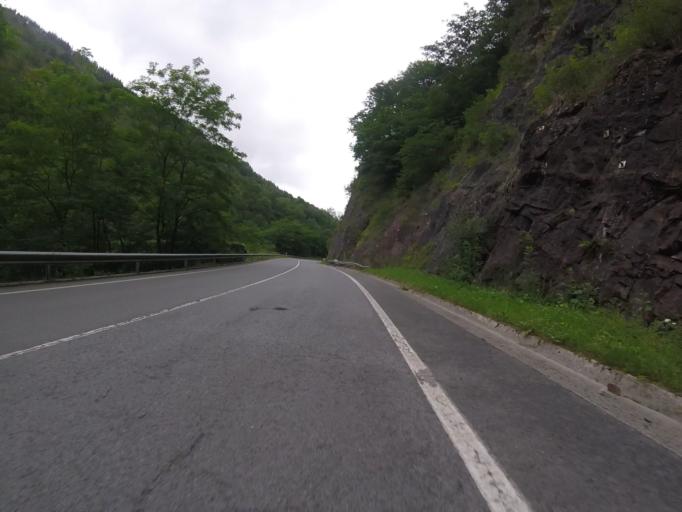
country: ES
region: Navarre
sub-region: Provincia de Navarra
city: Zubieta
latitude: 43.1118
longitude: -1.7622
